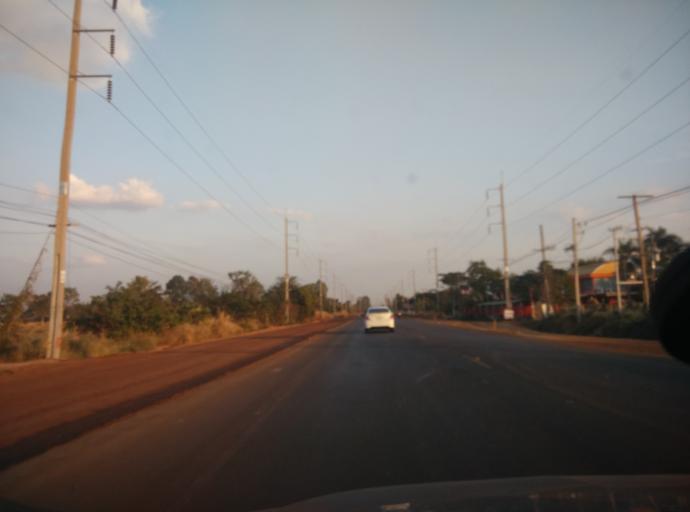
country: TH
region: Sisaket
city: Si Sa Ket
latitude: 15.1393
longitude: 104.2620
